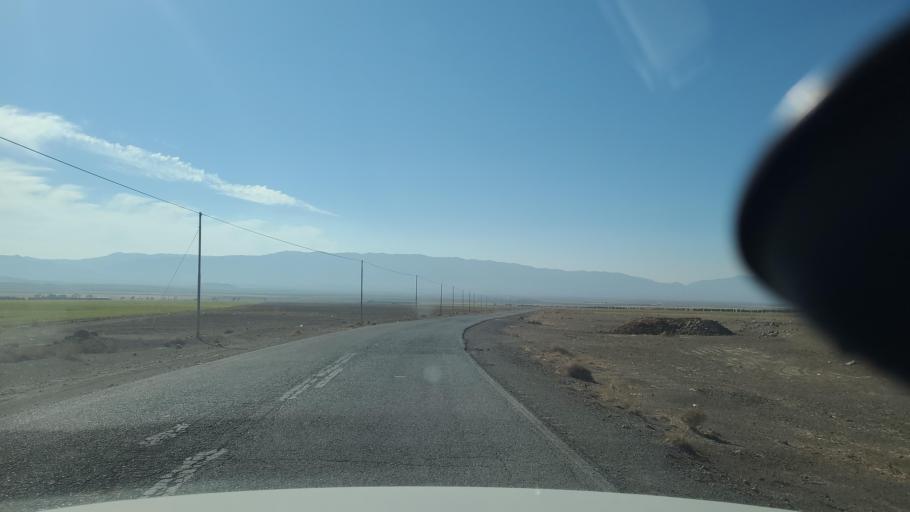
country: IR
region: Razavi Khorasan
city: Dowlatabad
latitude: 35.6151
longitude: 59.4737
